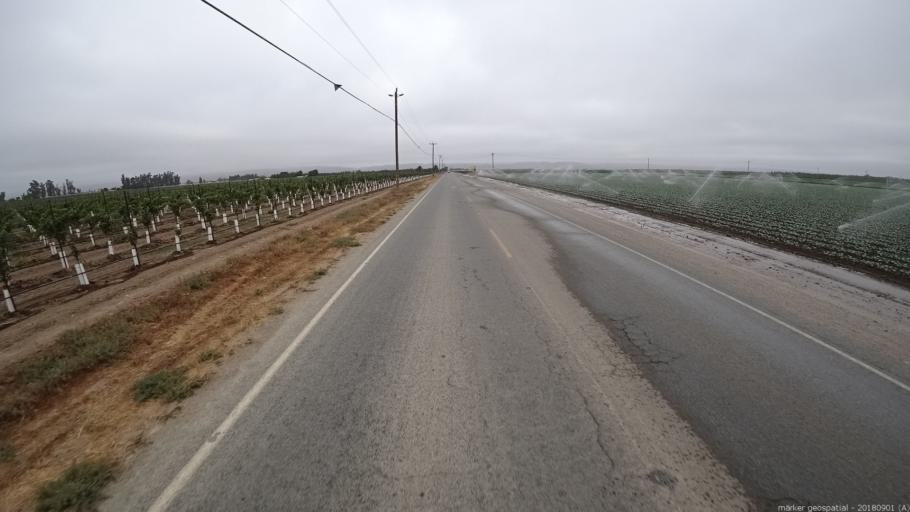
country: US
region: California
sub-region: Monterey County
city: Greenfield
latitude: 36.3016
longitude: -121.2700
